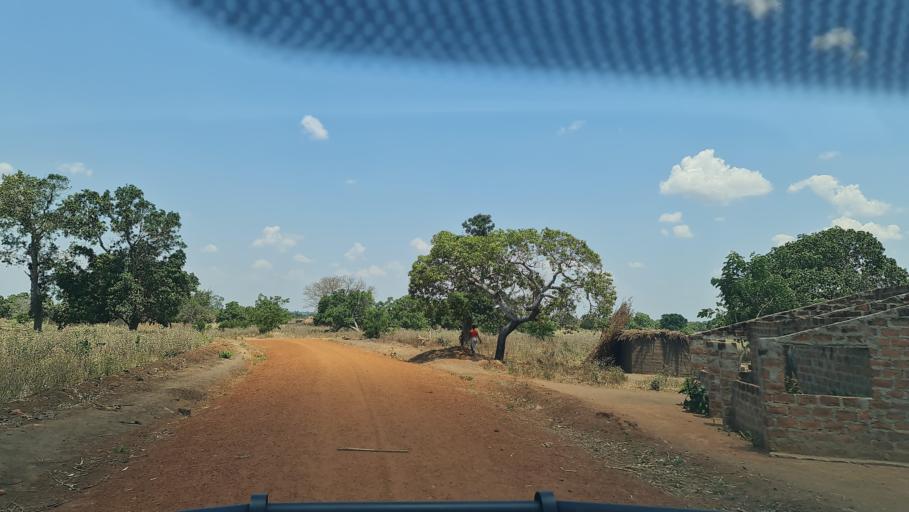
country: MZ
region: Nampula
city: Nacala
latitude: -14.8162
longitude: 40.0686
